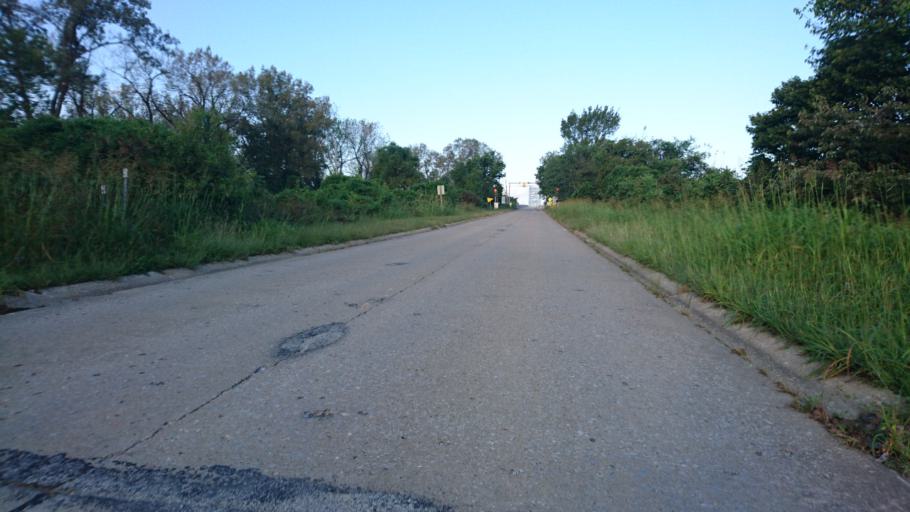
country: US
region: Illinois
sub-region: Madison County
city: Mitchell
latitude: 38.7621
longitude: -90.1321
